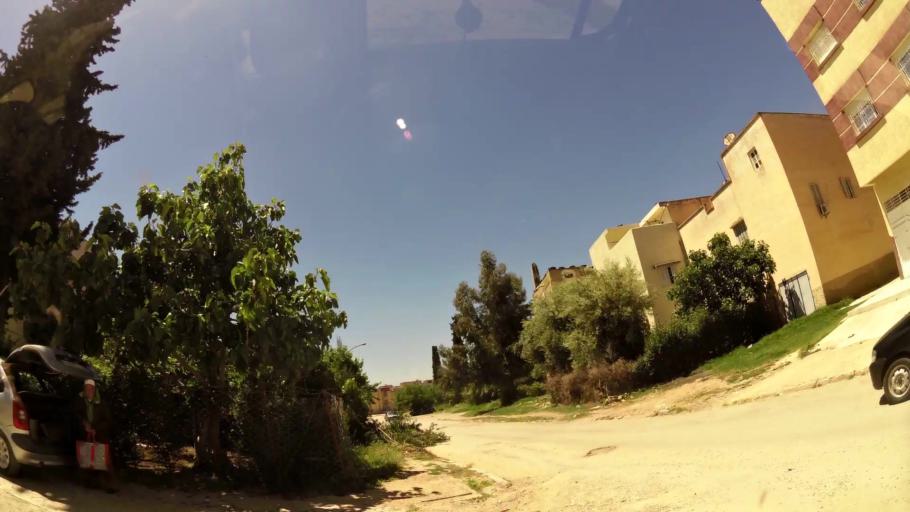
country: MA
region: Meknes-Tafilalet
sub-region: Meknes
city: Meknes
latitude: 33.8786
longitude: -5.5670
